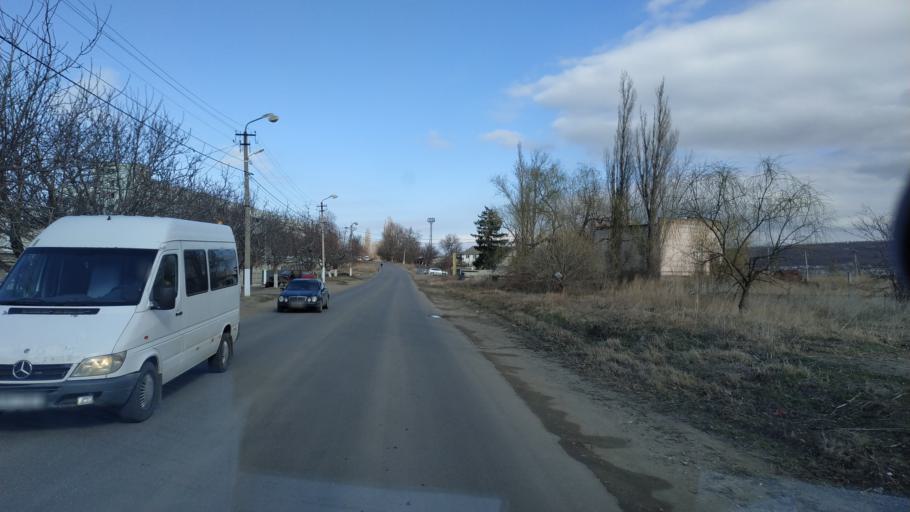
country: MD
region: Causeni
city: Causeni
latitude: 46.6565
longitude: 29.4161
